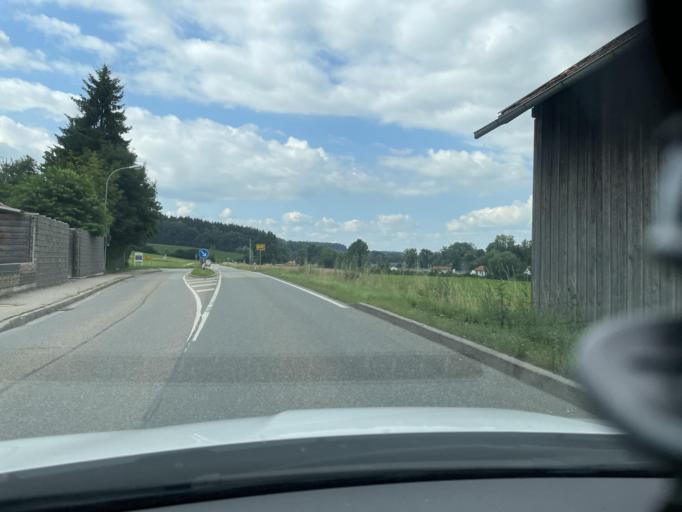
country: DE
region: Bavaria
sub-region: Upper Bavaria
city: Sankt Wolfgang
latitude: 48.2230
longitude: 12.1358
